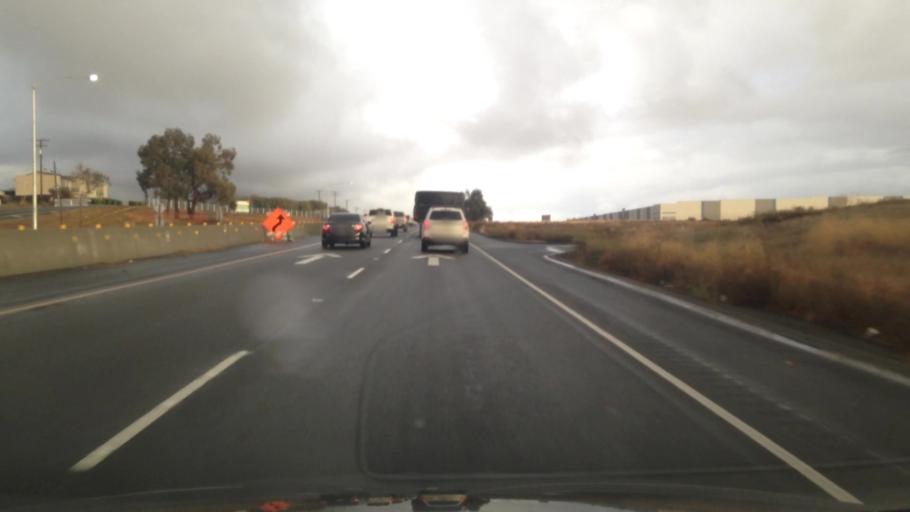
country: US
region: California
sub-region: Riverside County
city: Beaumont
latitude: 33.9335
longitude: -117.0087
